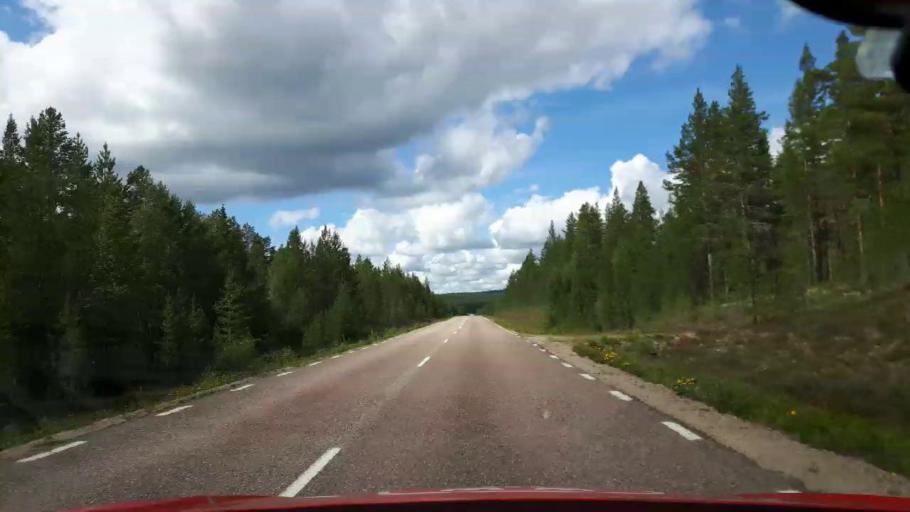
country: SE
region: Jaemtland
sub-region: Harjedalens Kommun
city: Sveg
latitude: 61.8332
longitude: 13.9224
